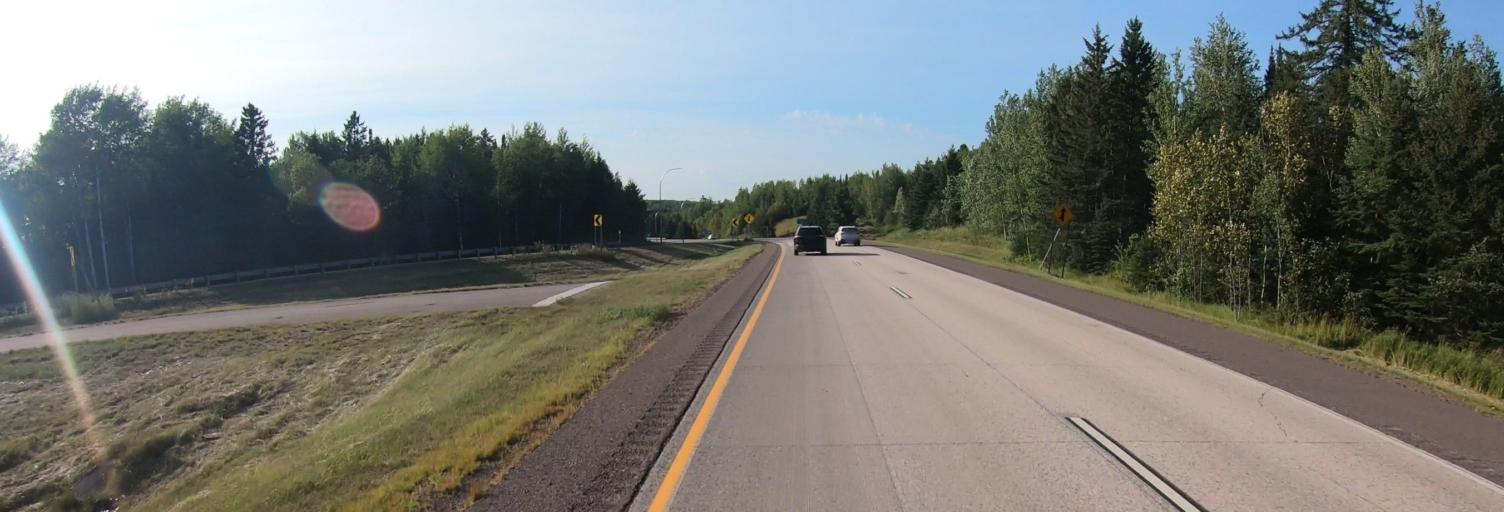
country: US
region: Minnesota
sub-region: Carlton County
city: Cloquet
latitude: 46.9559
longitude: -92.4552
